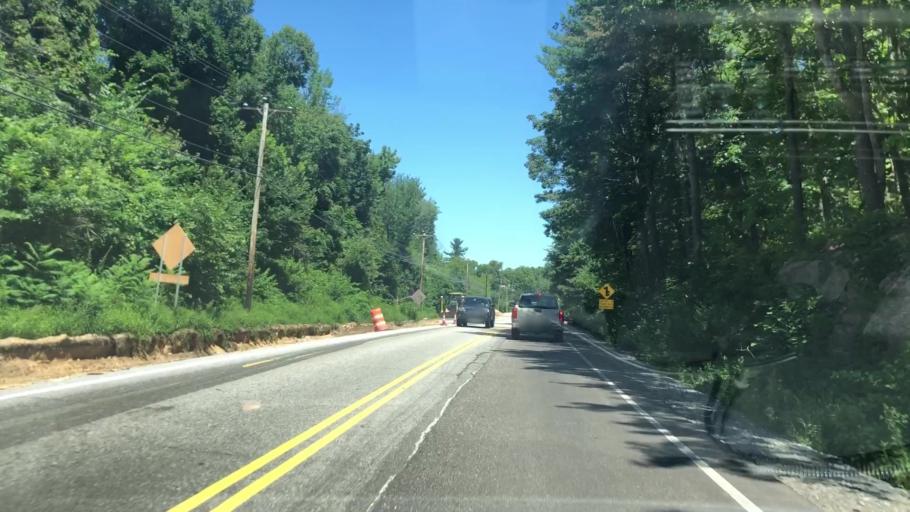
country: US
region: New Hampshire
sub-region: Hillsborough County
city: Bedford
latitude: 42.9516
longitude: -71.5112
